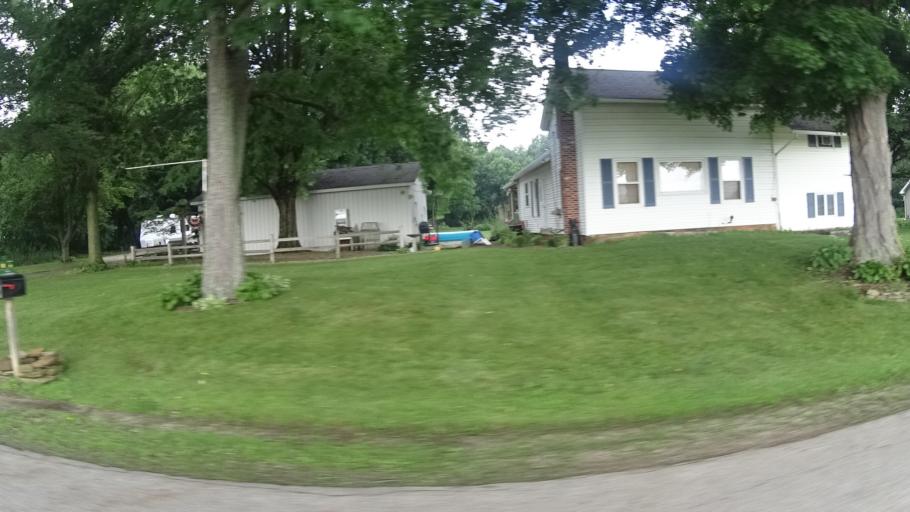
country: US
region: Ohio
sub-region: Huron County
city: Wakeman
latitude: 41.2973
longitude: -82.4428
